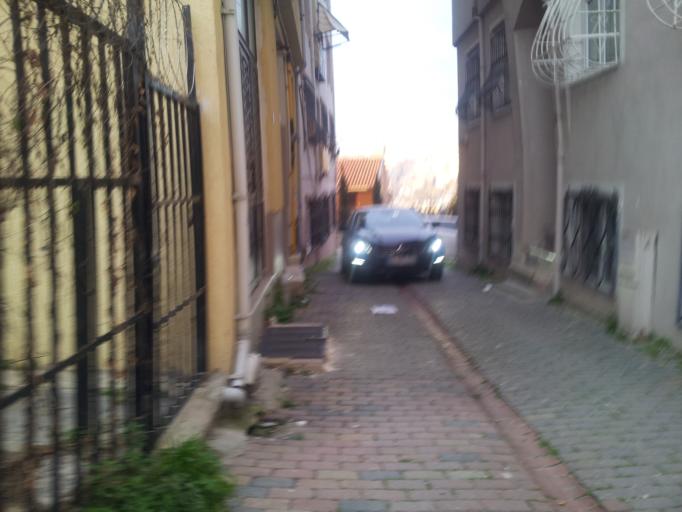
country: TR
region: Istanbul
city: Istanbul
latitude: 41.0379
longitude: 28.9417
